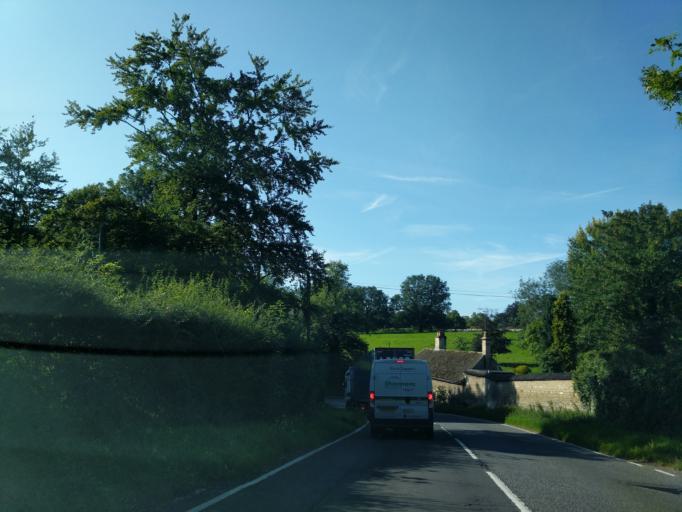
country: GB
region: England
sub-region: Lincolnshire
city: Bourne
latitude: 52.7952
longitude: -0.4504
